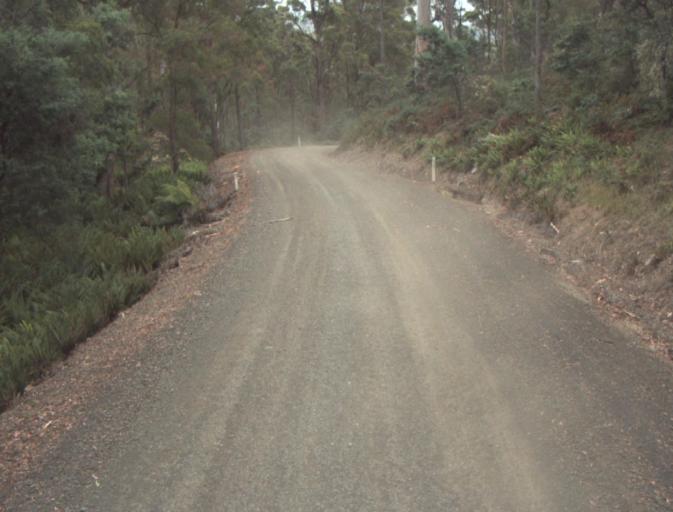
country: AU
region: Tasmania
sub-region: Northern Midlands
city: Evandale
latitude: -41.4873
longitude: 147.5419
